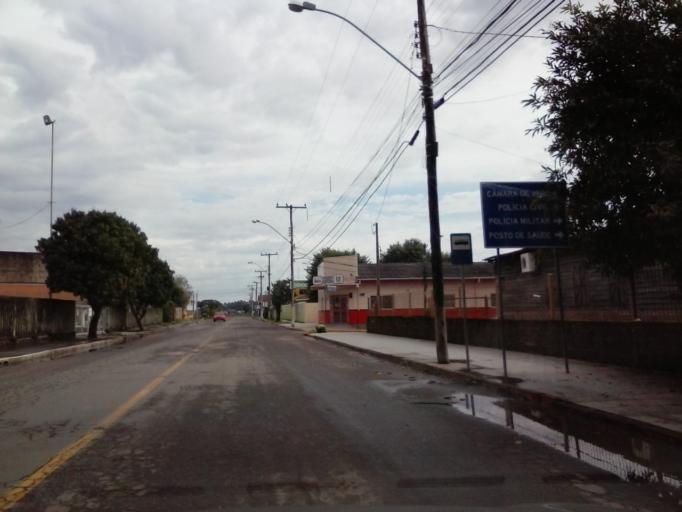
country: BR
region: Rio Grande do Sul
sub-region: Porto Alegre
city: Porto Alegre
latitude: -29.9979
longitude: -51.3148
